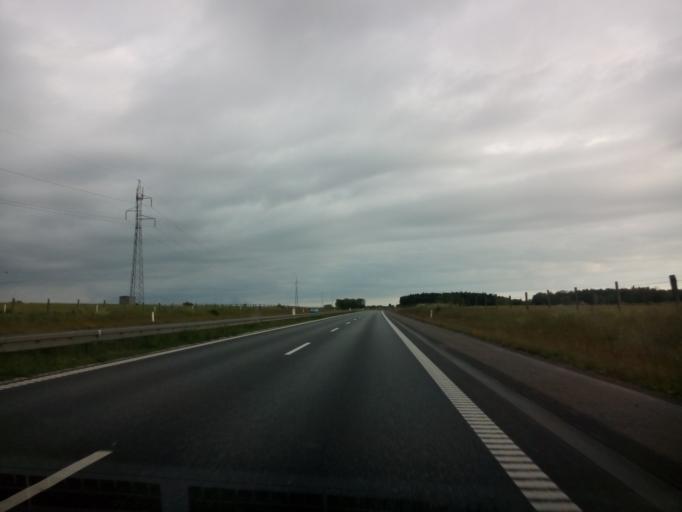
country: DK
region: North Denmark
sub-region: Hjorring Kommune
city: Vra
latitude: 57.3284
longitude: 10.0252
